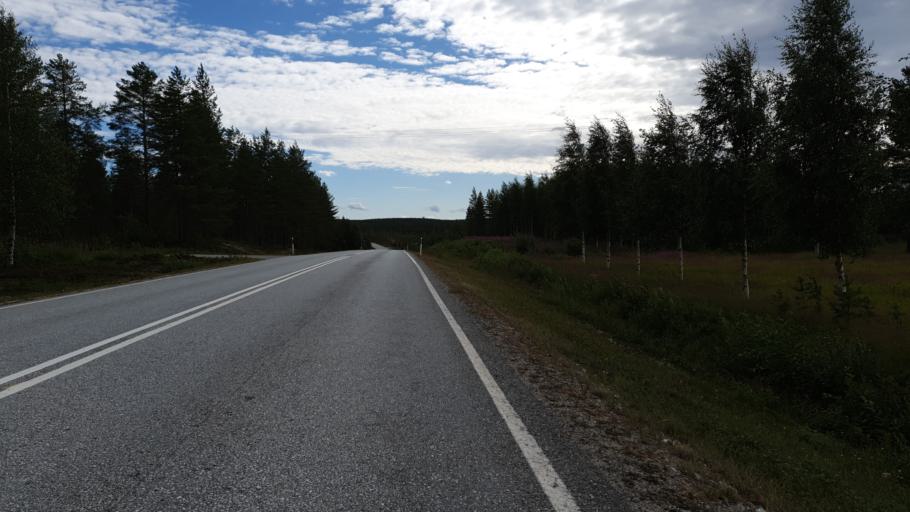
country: FI
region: Kainuu
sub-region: Kehys-Kainuu
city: Kuhmo
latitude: 64.4844
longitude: 29.7931
